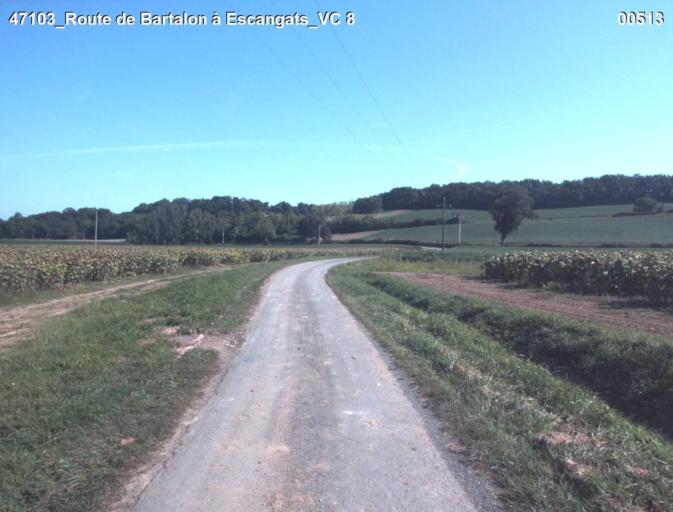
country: FR
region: Aquitaine
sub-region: Departement du Lot-et-Garonne
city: Nerac
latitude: 44.0900
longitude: 0.3157
